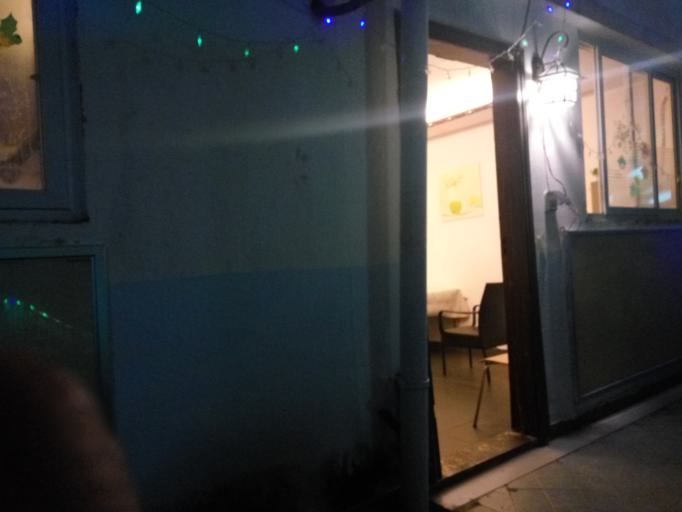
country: CN
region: Hainan
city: Sanya
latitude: 18.2248
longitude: 109.5170
